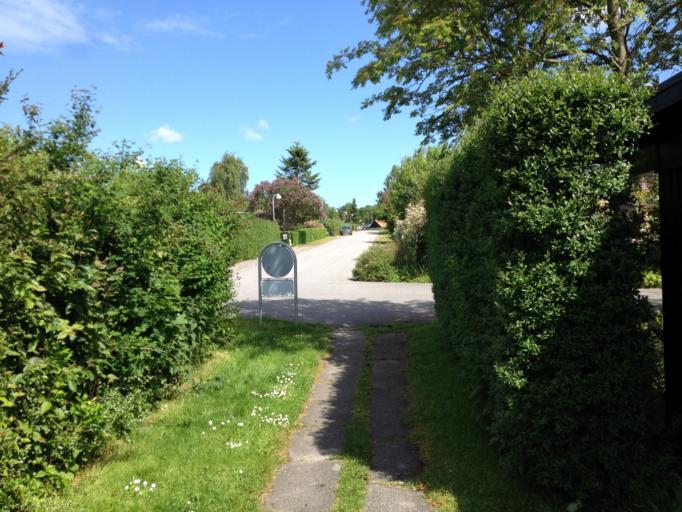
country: DK
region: Capital Region
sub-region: Fredensborg Kommune
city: Niva
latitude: 55.9333
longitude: 12.4921
